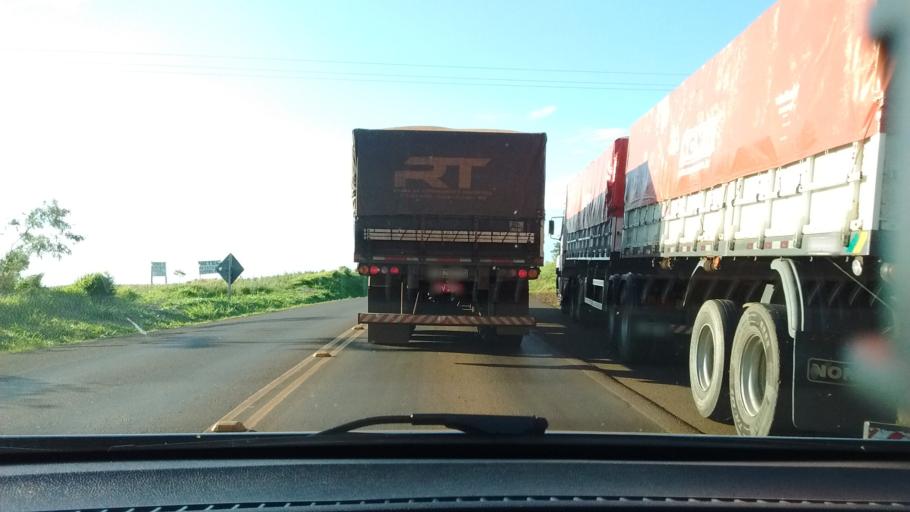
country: BR
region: Parana
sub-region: Cascavel
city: Cascavel
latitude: -25.2252
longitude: -53.5919
